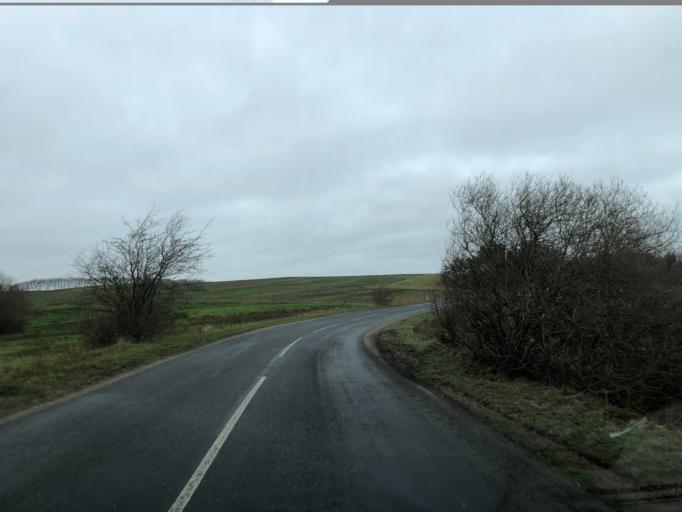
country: DK
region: Central Jutland
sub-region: Viborg Kommune
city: Stoholm
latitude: 56.4359
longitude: 9.1058
